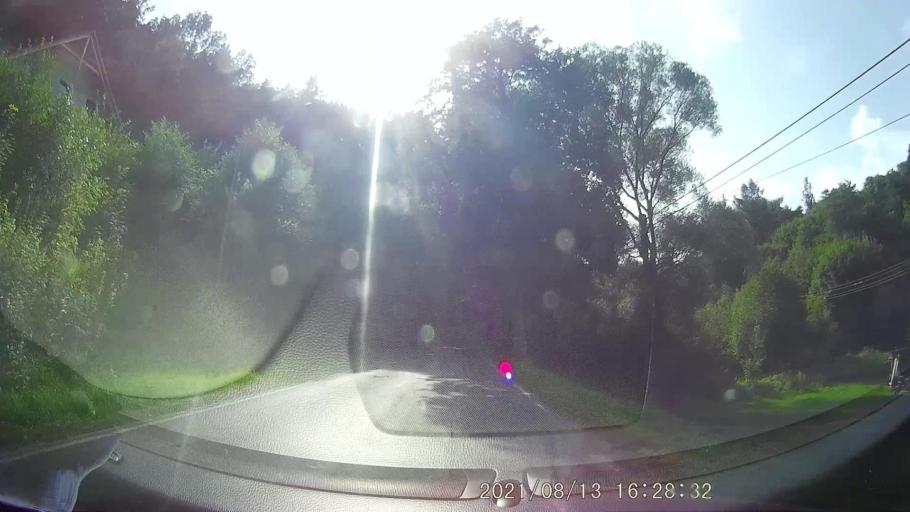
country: PL
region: Lower Silesian Voivodeship
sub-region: Powiat klodzki
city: Kudowa-Zdroj
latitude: 50.4458
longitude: 16.2604
